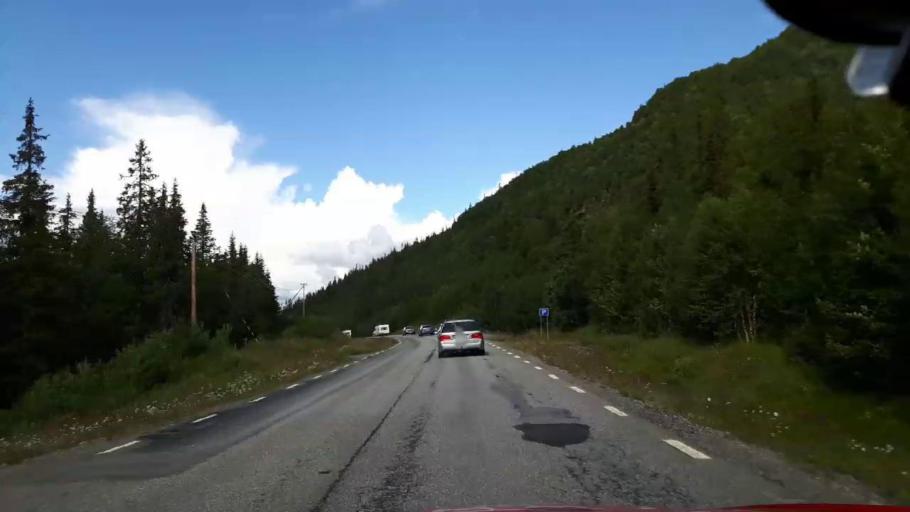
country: SE
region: Vaesterbotten
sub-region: Vilhelmina Kommun
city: Sjoberg
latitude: 65.0367
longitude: 15.1324
